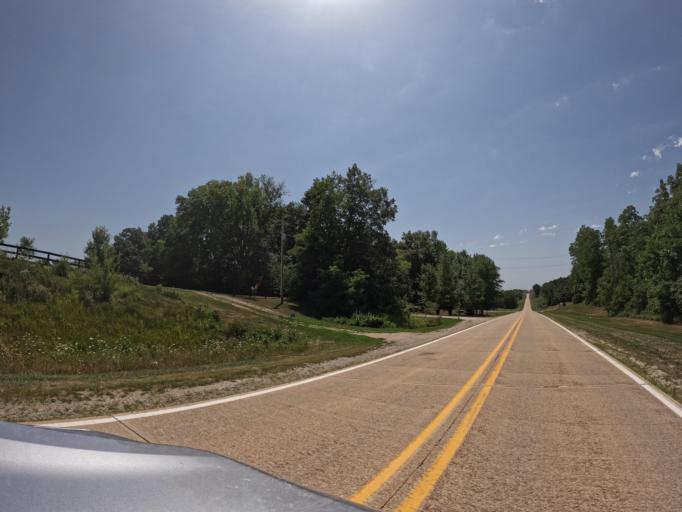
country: US
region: Iowa
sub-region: Henry County
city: Mount Pleasant
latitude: 40.9453
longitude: -91.5546
